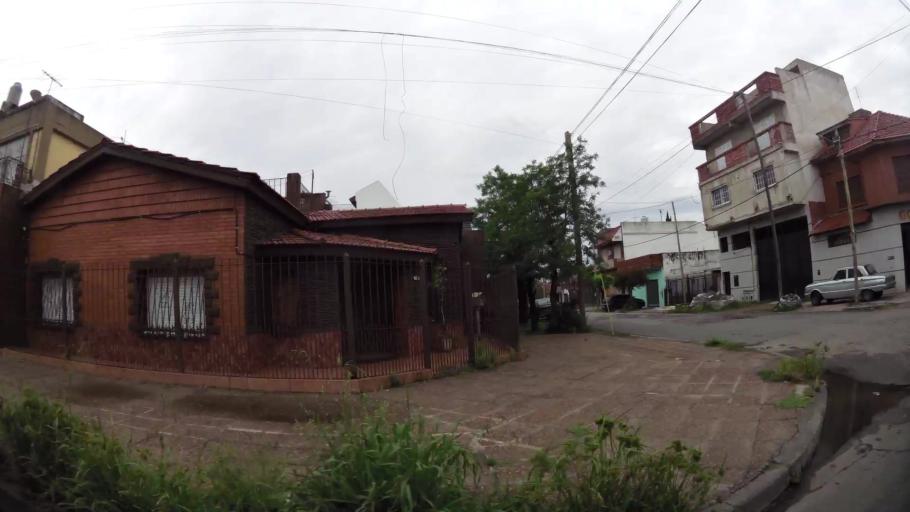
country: AR
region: Buenos Aires
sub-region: Partido de Lanus
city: Lanus
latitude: -34.7258
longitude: -58.3653
